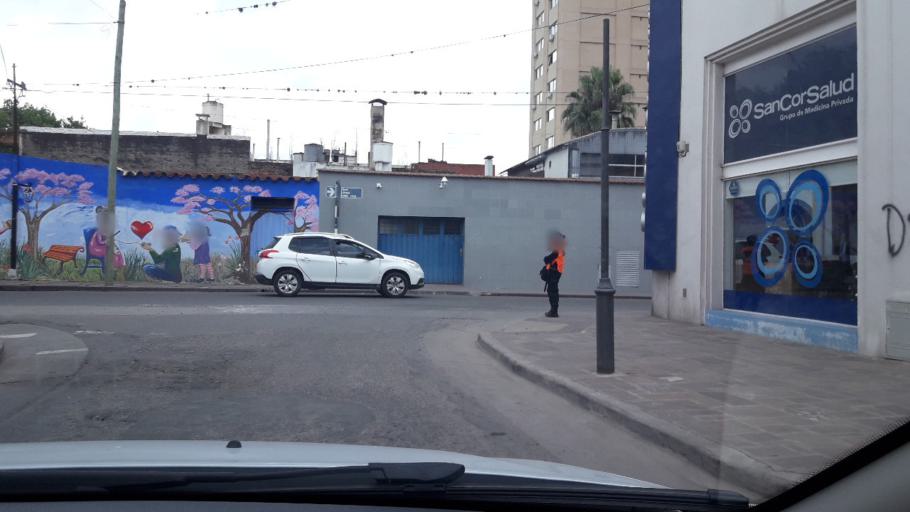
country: AR
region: Jujuy
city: San Salvador de Jujuy
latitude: -24.1847
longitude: -65.3125
